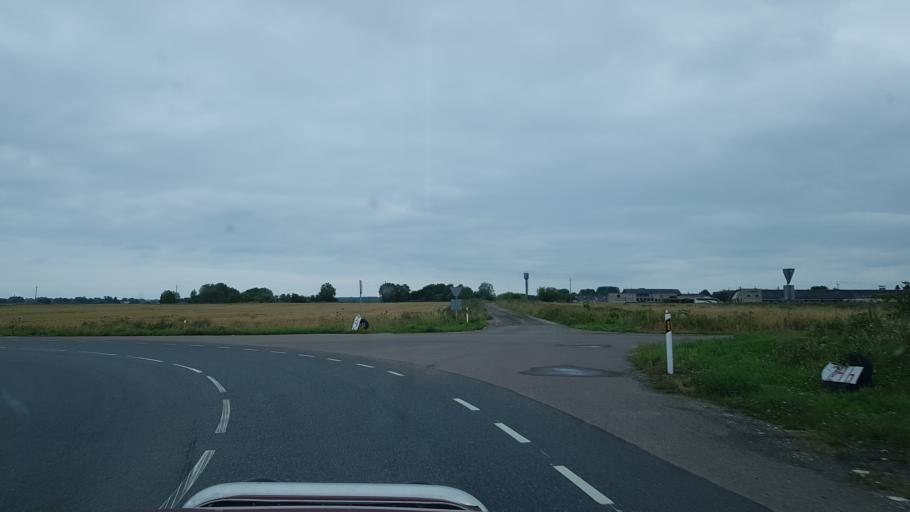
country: EE
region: Ida-Virumaa
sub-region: Johvi vald
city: Johvi
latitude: 59.3316
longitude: 27.3755
